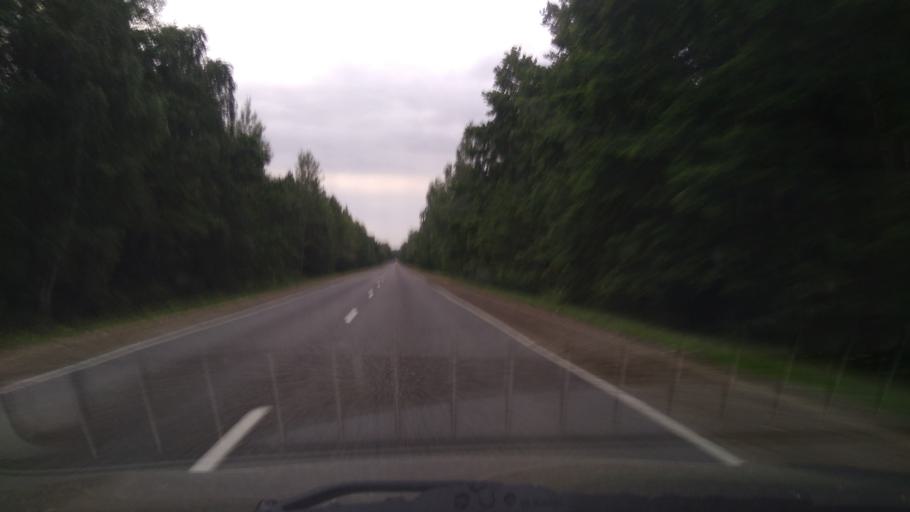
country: BY
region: Brest
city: Byaroza
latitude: 52.4068
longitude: 24.9982
